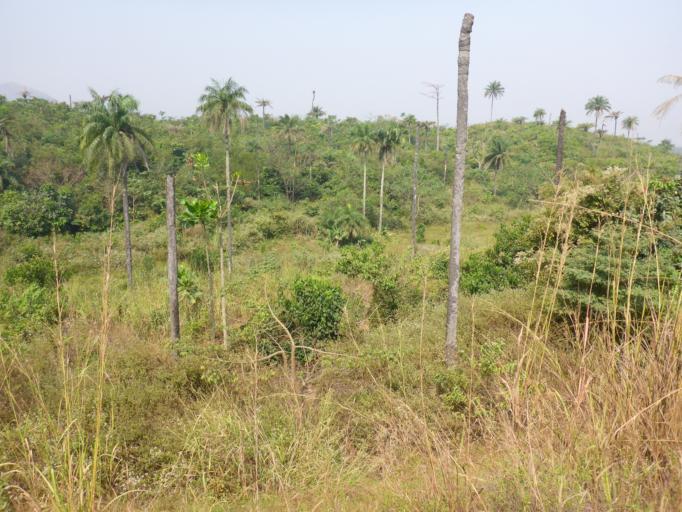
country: SL
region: Northern Province
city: Bumbuna
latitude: 8.9573
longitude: -11.7563
